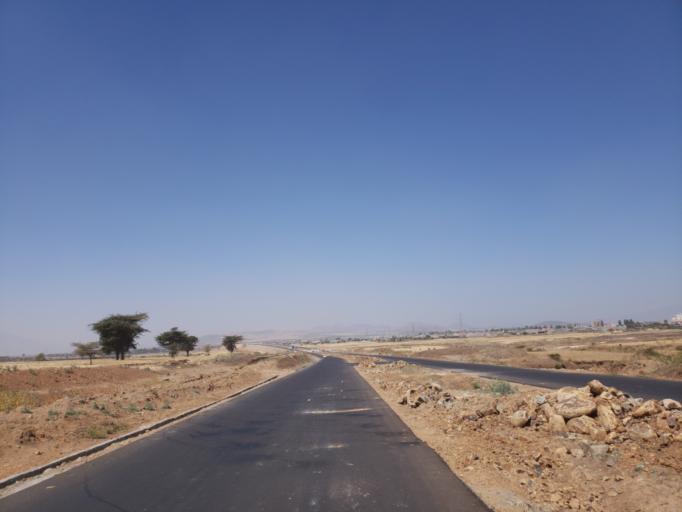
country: ET
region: Oromiya
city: Mojo
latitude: 8.5666
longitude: 39.1512
